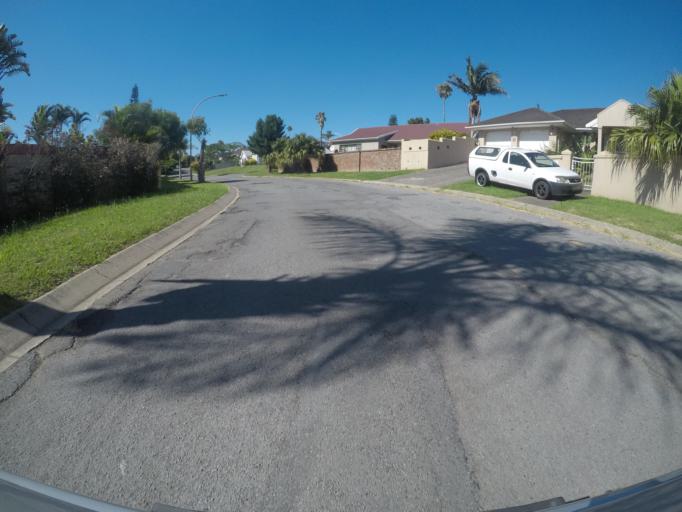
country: ZA
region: Eastern Cape
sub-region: Buffalo City Metropolitan Municipality
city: East London
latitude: -32.9479
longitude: 27.9010
